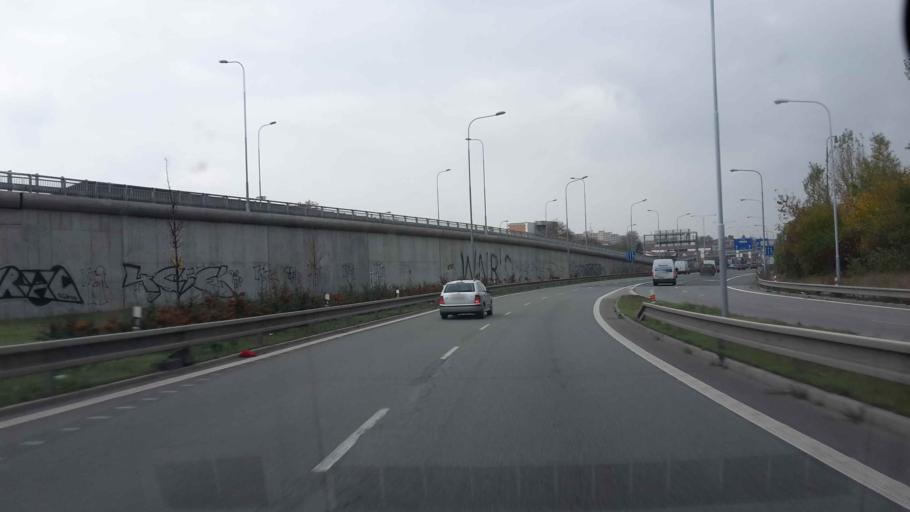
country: CZ
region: South Moravian
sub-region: Mesto Brno
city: Brno
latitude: 49.2213
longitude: 16.6030
